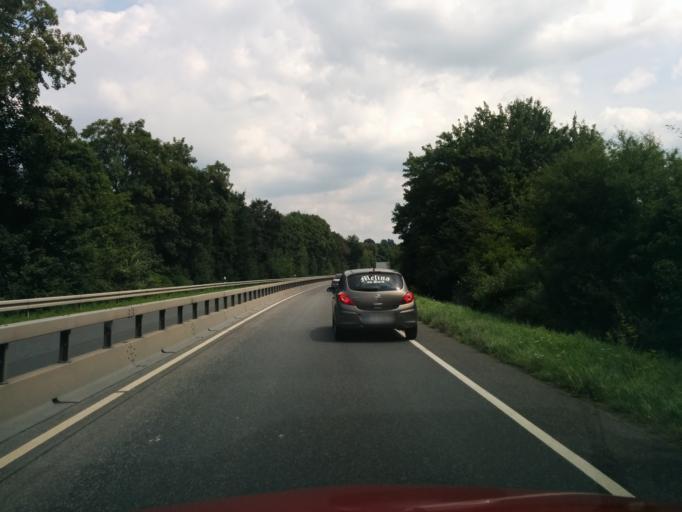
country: DE
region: Hesse
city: Leun
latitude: 50.5473
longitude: 8.3396
